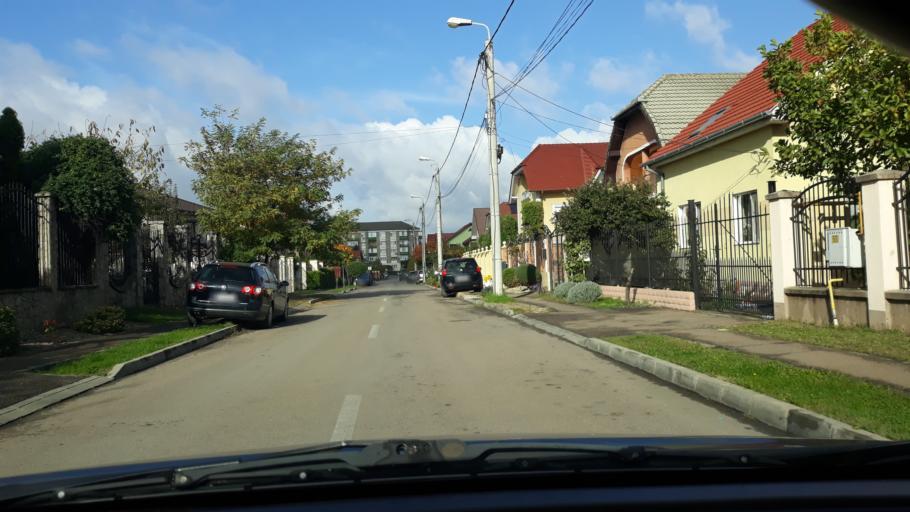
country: RO
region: Bihor
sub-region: Comuna Sanmartin
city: Sanmartin
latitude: 47.0285
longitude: 21.9502
